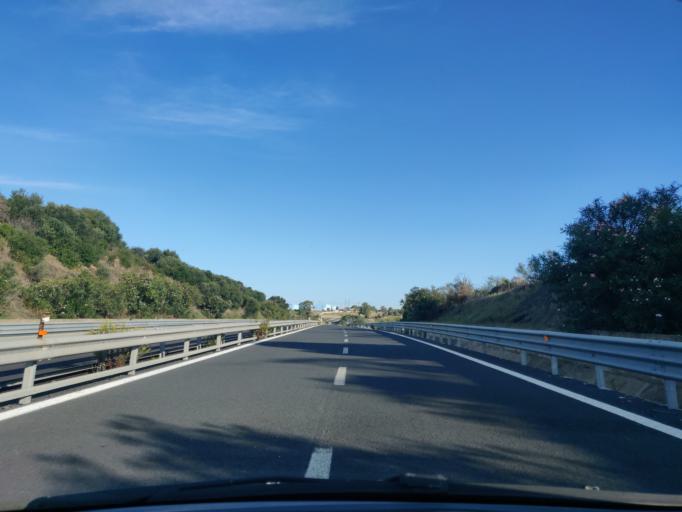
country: IT
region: Latium
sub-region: Citta metropolitana di Roma Capitale
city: Civitavecchia
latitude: 42.1146
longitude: 11.7923
